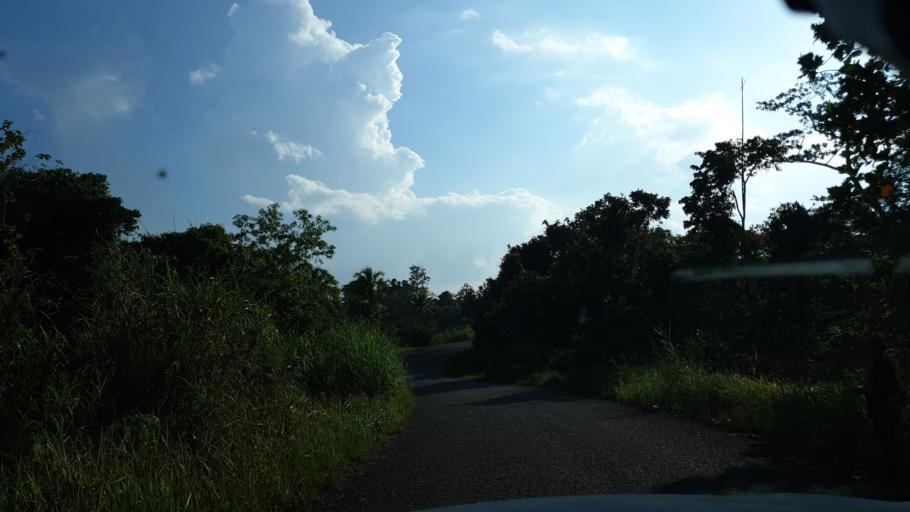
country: PG
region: East Sepik
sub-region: Wewak
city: Wewak
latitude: -3.6995
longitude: 143.6451
